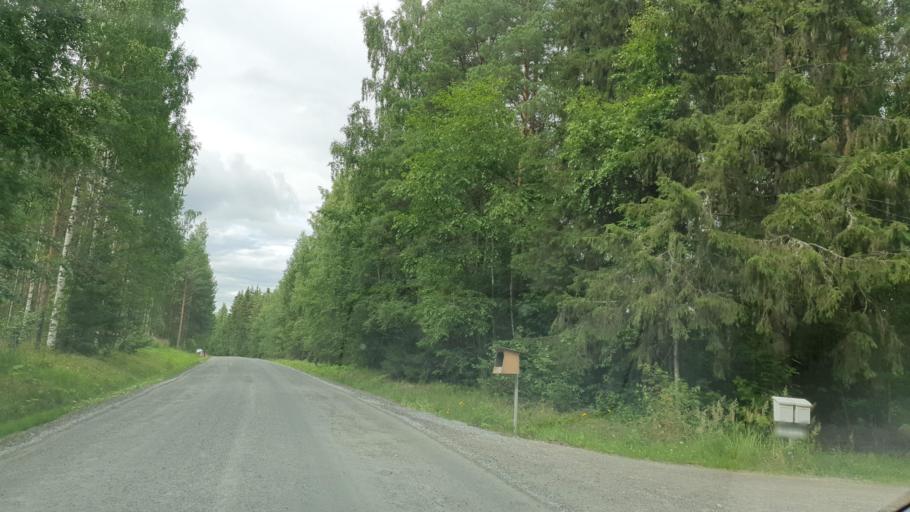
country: FI
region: Northern Savo
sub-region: Ylae-Savo
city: Iisalmi
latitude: 63.5314
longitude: 27.0886
